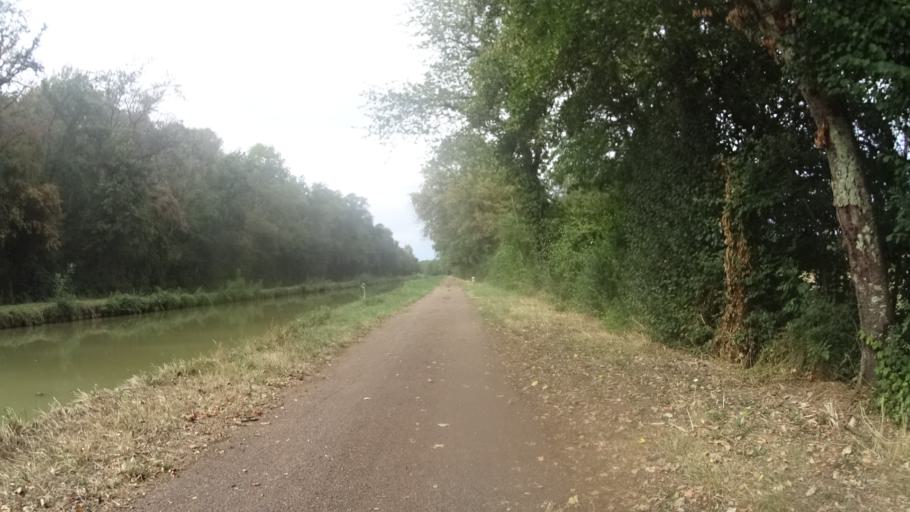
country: FR
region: Bourgogne
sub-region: Departement de la Nievre
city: Sermoise-sur-Loire
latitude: 46.9526
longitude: 3.2002
